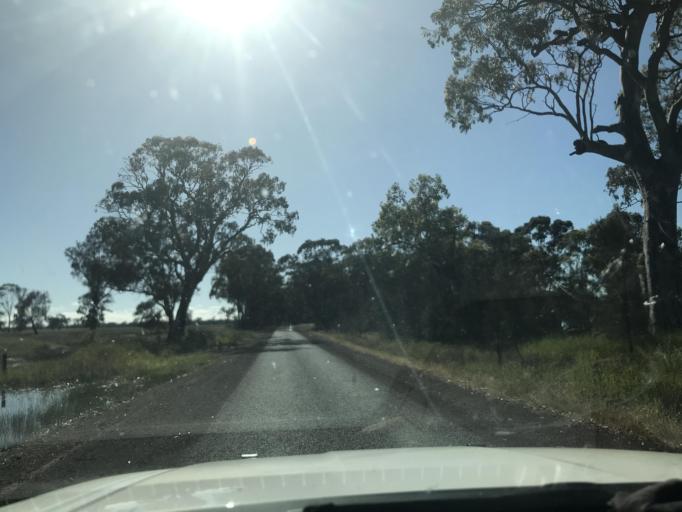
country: AU
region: Victoria
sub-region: Horsham
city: Horsham
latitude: -37.0085
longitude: 141.6558
